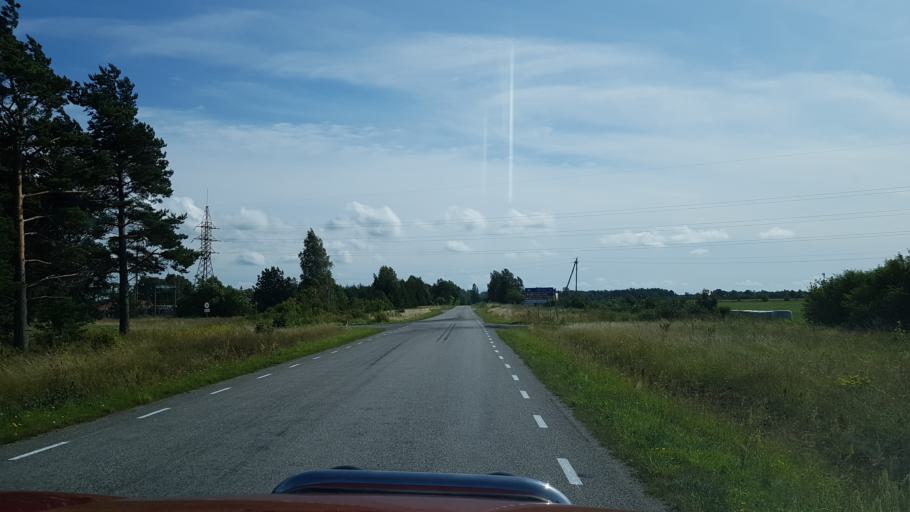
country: EE
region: Laeaene
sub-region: Lihula vald
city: Lihula
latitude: 58.4515
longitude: 23.7409
